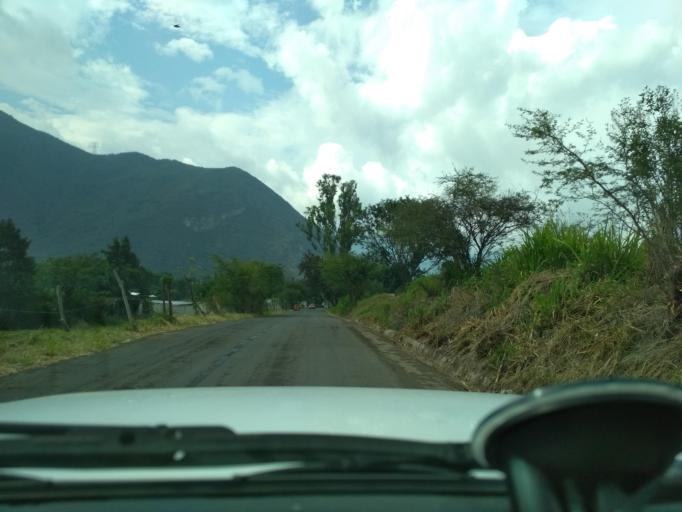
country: MX
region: Veracruz
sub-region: Nogales
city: Taza de Agua Ojo Zarco
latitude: 18.7833
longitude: -97.2004
